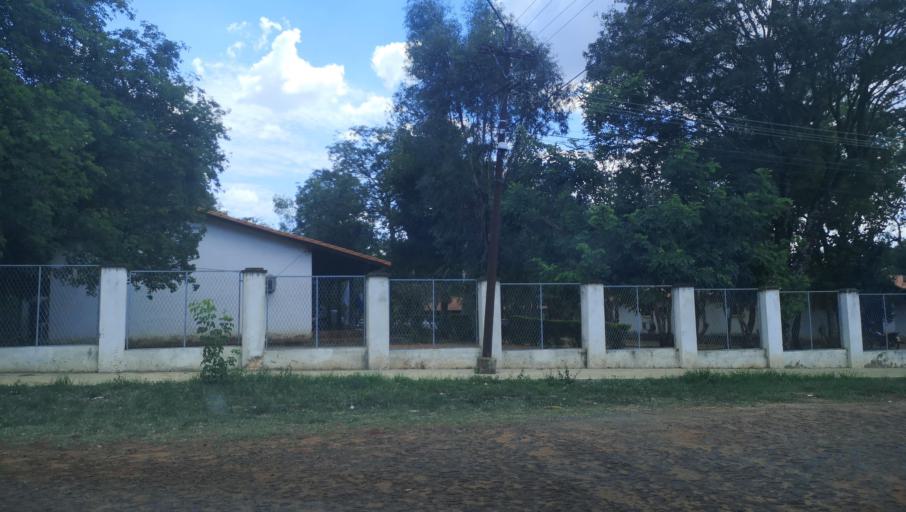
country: PY
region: Misiones
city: Santa Maria
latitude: -26.8900
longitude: -57.0322
